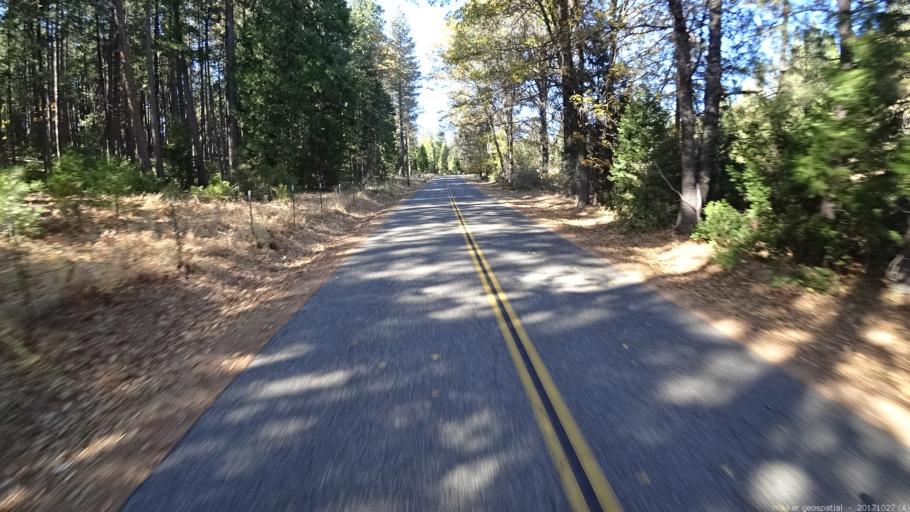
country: US
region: California
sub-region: Shasta County
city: Shingletown
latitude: 40.6875
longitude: -121.9094
